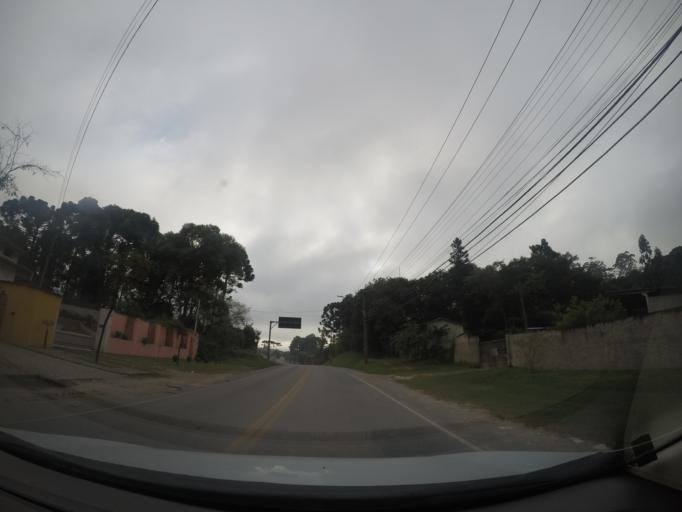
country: BR
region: Parana
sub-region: Colombo
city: Colombo
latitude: -25.2947
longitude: -49.2320
